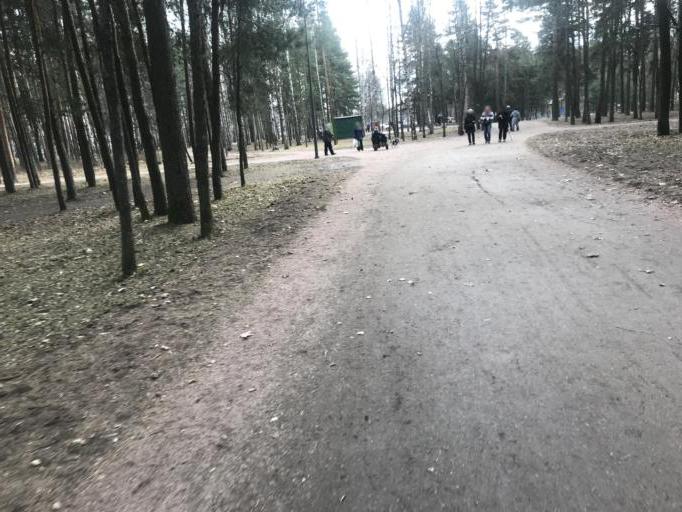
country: RU
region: St.-Petersburg
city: Sosnovka
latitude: 60.0151
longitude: 30.3508
